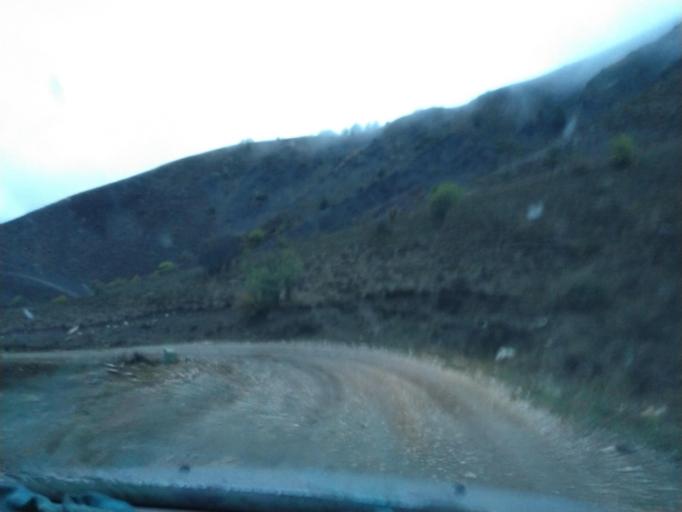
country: RU
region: North Ossetia
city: Tarskoye
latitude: 42.8238
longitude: 44.9692
